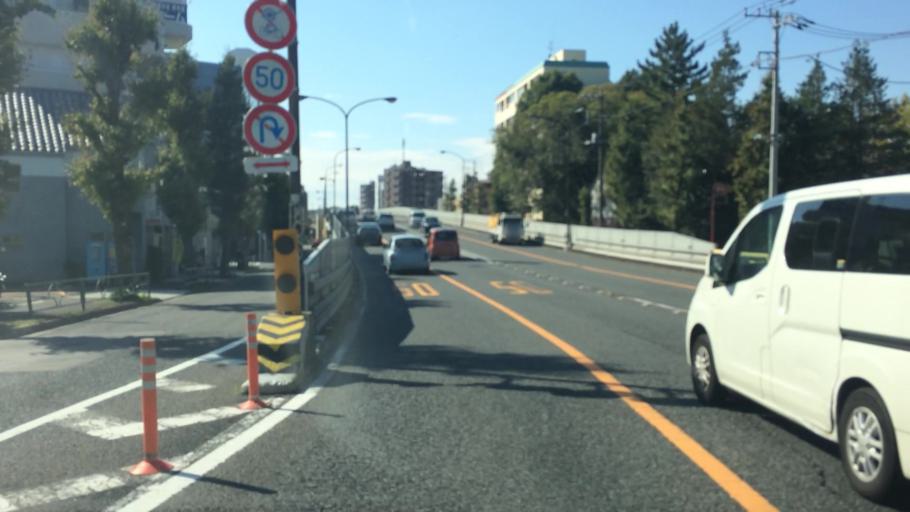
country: JP
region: Tokyo
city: Tokyo
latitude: 35.6099
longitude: 139.6507
